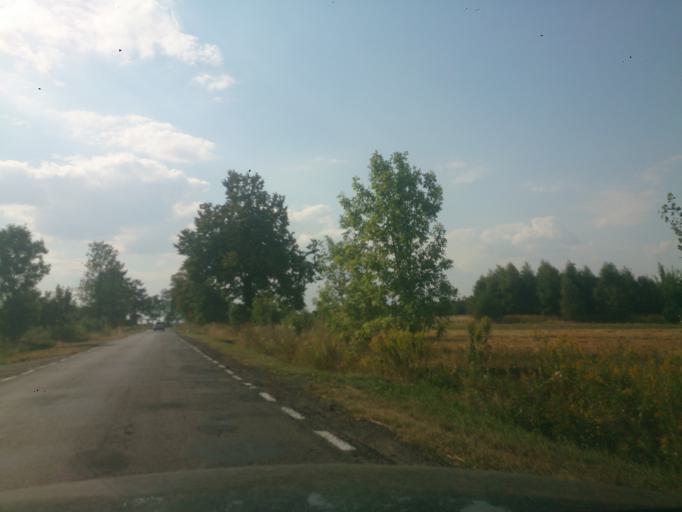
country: PL
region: Swietokrzyskie
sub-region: Powiat opatowski
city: Iwaniska
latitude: 50.6932
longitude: 21.3477
